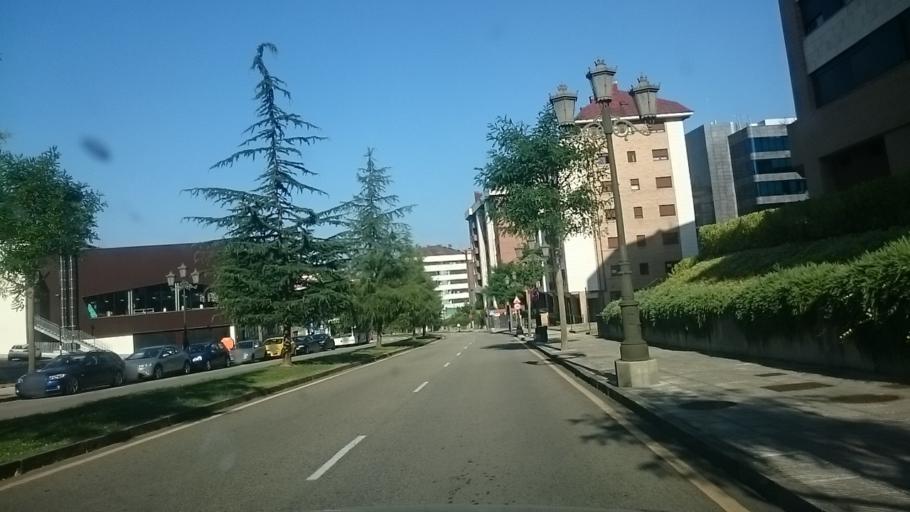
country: ES
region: Asturias
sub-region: Province of Asturias
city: Oviedo
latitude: 43.3520
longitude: -5.8636
